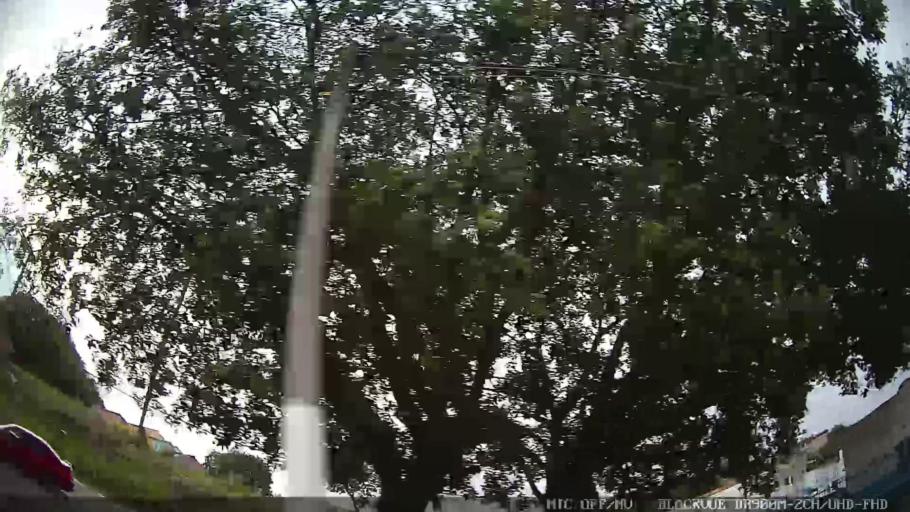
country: BR
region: Sao Paulo
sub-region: Braganca Paulista
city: Braganca Paulista
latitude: -22.9406
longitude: -46.5405
